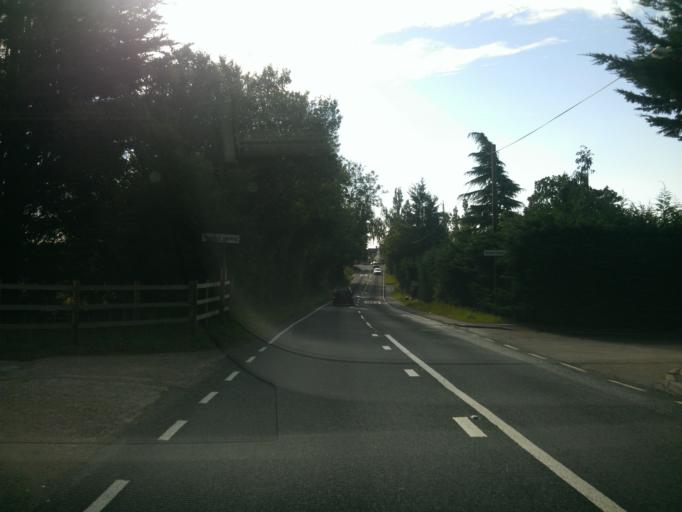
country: GB
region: England
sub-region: Essex
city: Alresford
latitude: 51.8442
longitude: 1.0232
